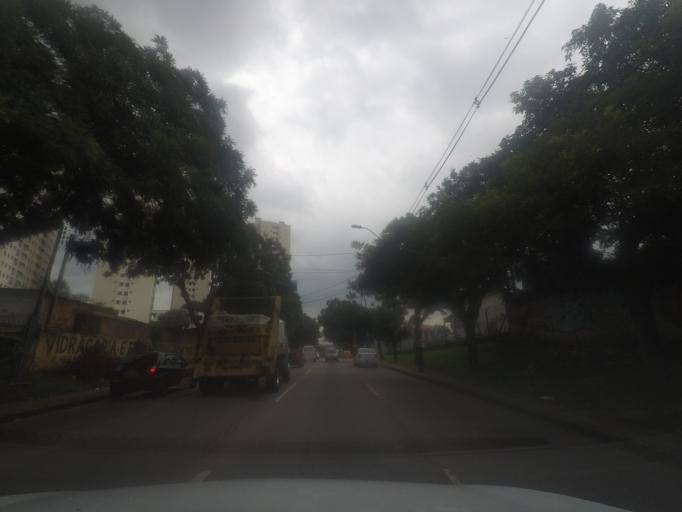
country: BR
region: Parana
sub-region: Curitiba
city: Curitiba
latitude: -25.4973
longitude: -49.2967
